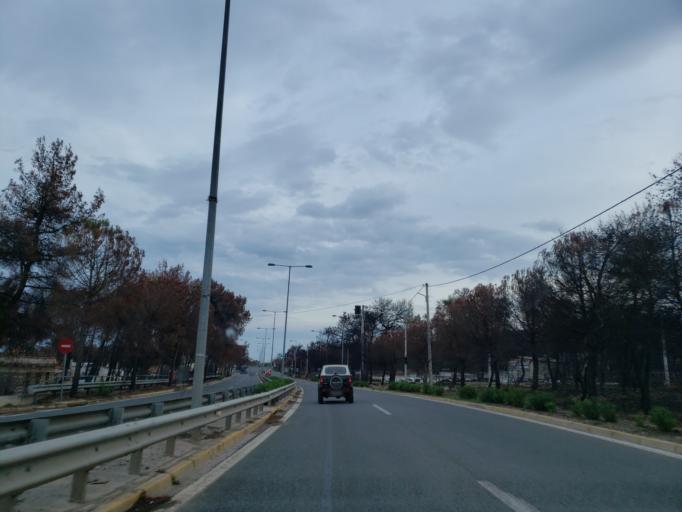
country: GR
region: Attica
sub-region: Nomarchia Anatolikis Attikis
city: Neos Voutzas
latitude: 38.0543
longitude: 23.9845
